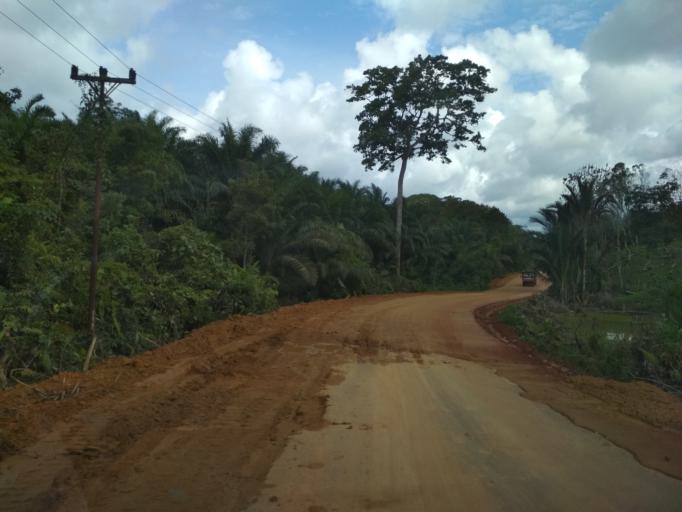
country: ID
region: West Kalimantan
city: Tayan
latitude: 0.5378
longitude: 110.0890
